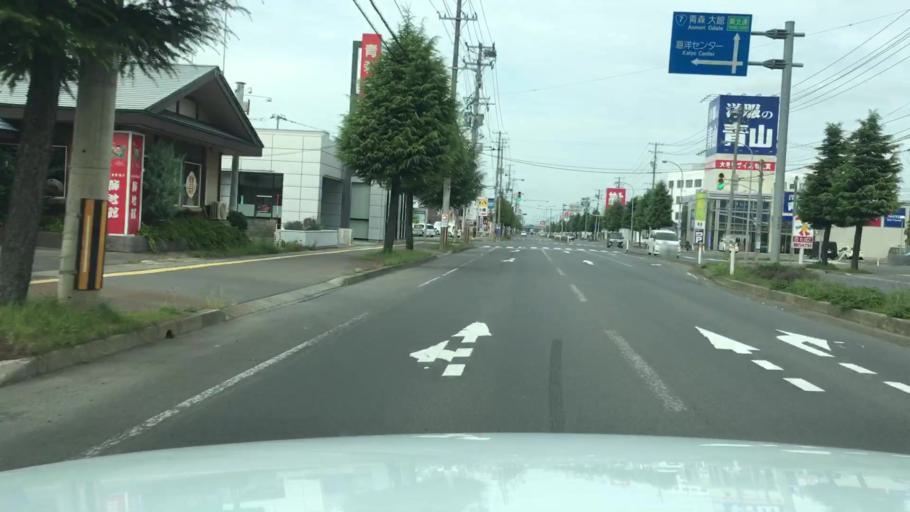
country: JP
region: Aomori
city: Hirosaki
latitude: 40.6139
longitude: 140.4836
